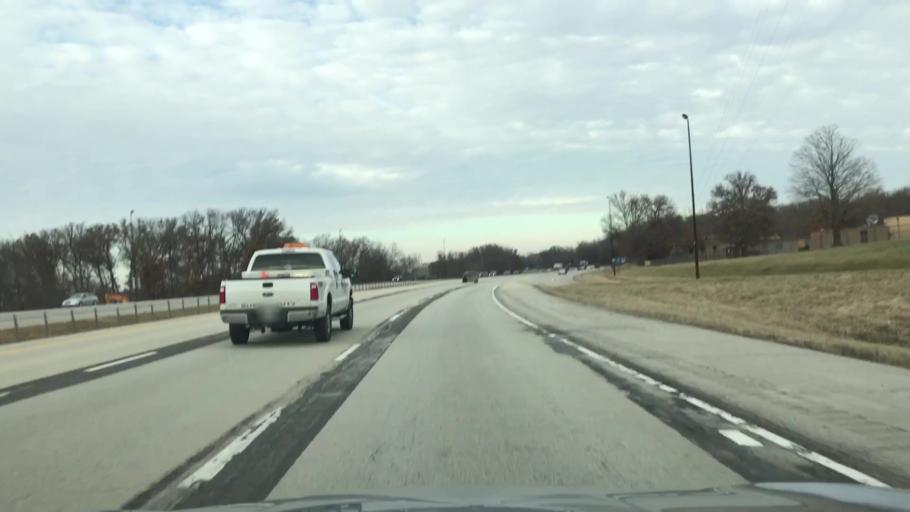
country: US
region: Illinois
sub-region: Sangamon County
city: Chatham
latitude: 39.6884
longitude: -89.6433
